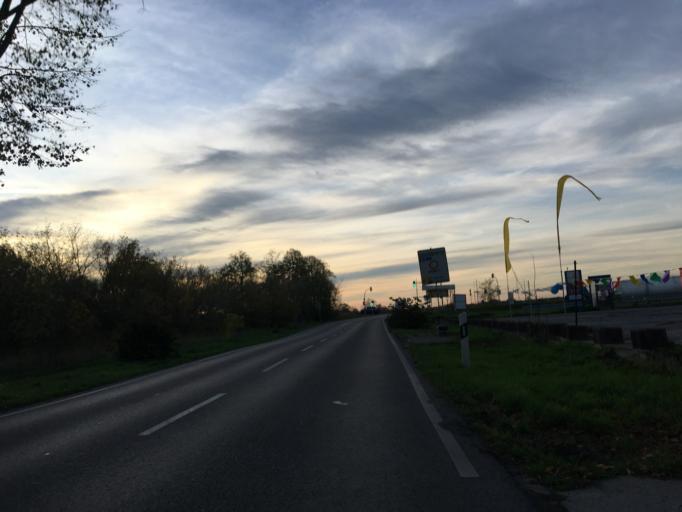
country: DE
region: Berlin
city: Blankenburg
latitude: 52.6177
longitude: 13.4507
